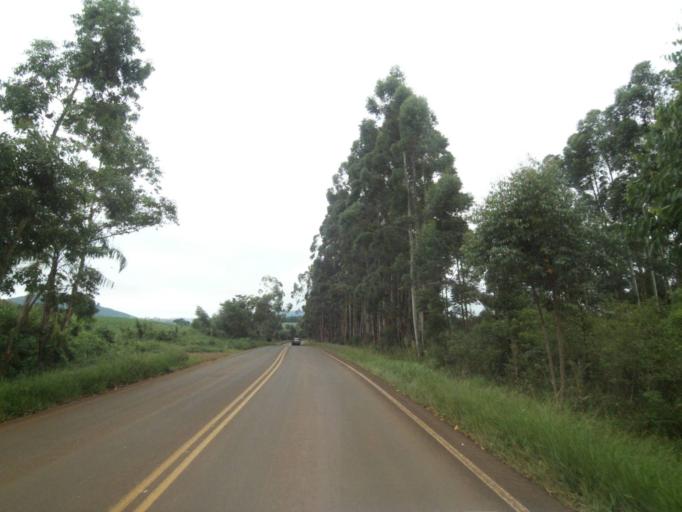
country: BR
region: Parana
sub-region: Pitanga
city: Pitanga
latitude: -24.9135
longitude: -51.8702
